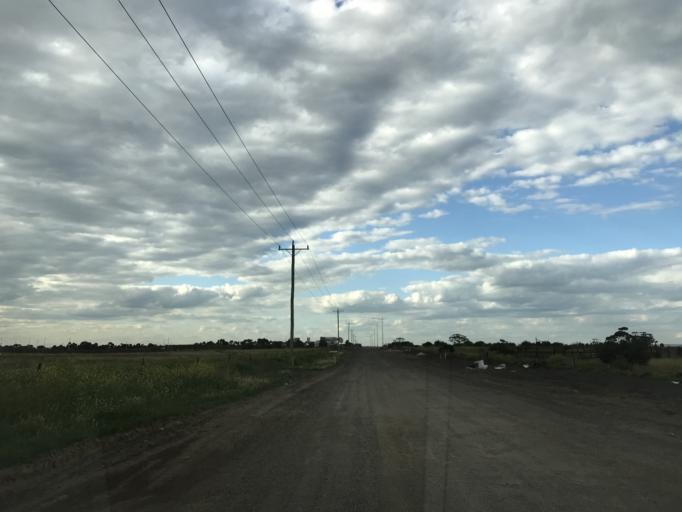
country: AU
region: Victoria
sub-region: Wyndham
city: Truganina
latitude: -37.8171
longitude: 144.7222
